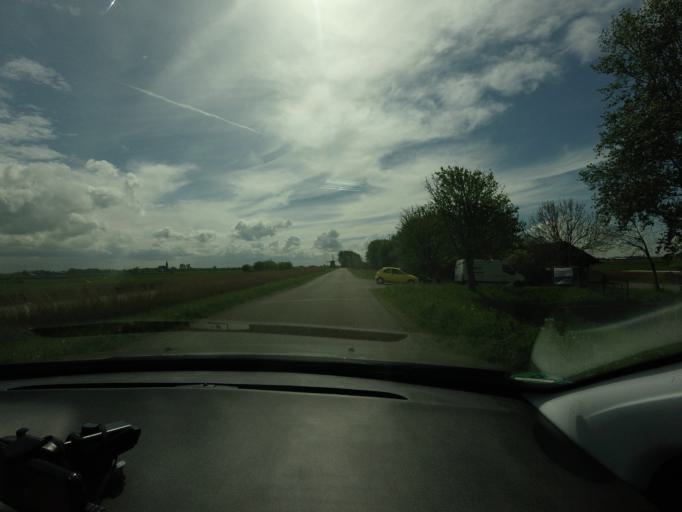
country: NL
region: North Holland
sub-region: Gemeente Heerhugowaard
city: Heerhugowaard
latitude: 52.6116
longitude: 4.8832
